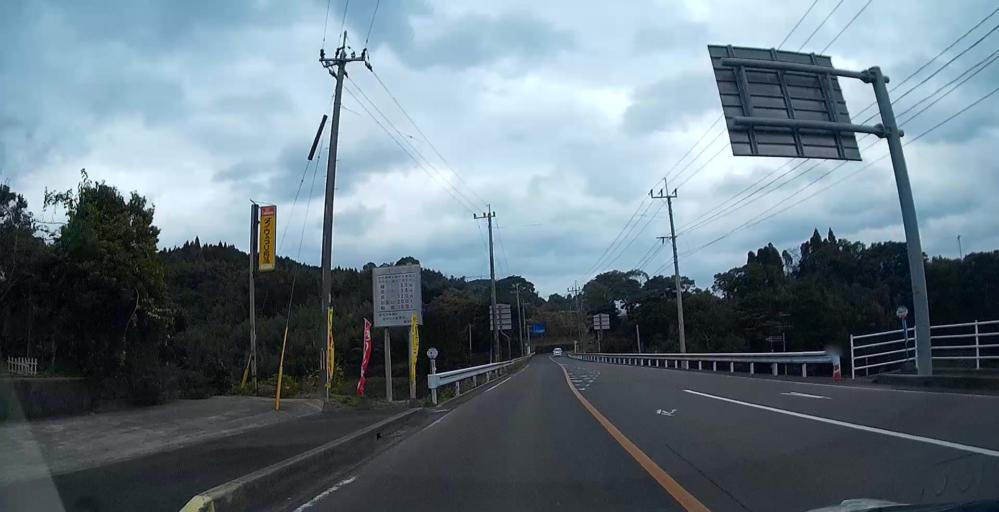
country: JP
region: Kagoshima
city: Akune
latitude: 32.1081
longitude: 130.1667
